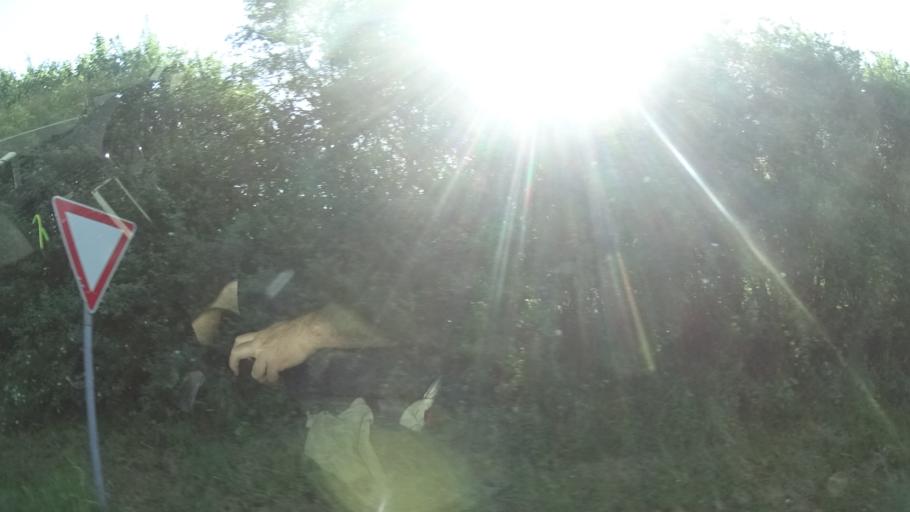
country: DE
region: Hesse
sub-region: Regierungsbezirk Giessen
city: Reiskirchen
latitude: 50.5919
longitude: 8.8322
